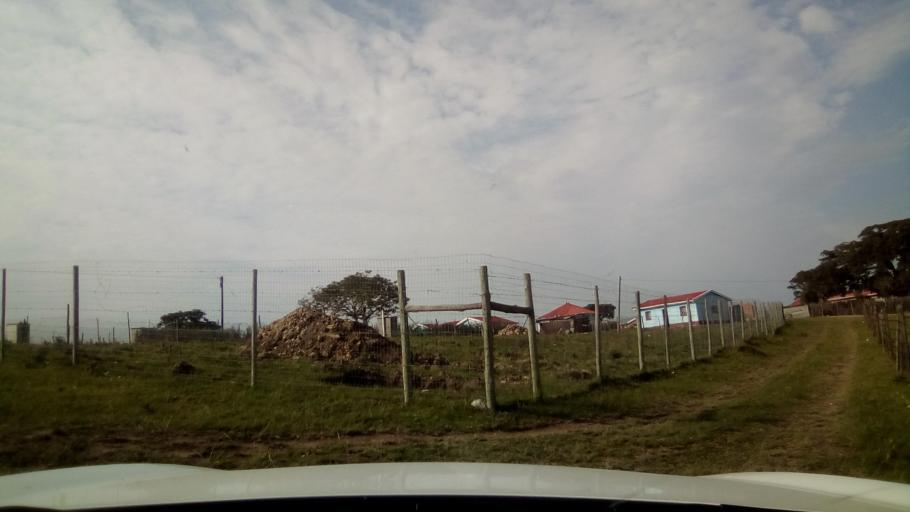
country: ZA
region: Eastern Cape
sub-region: Buffalo City Metropolitan Municipality
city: Bhisho
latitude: -33.0071
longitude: 27.3052
